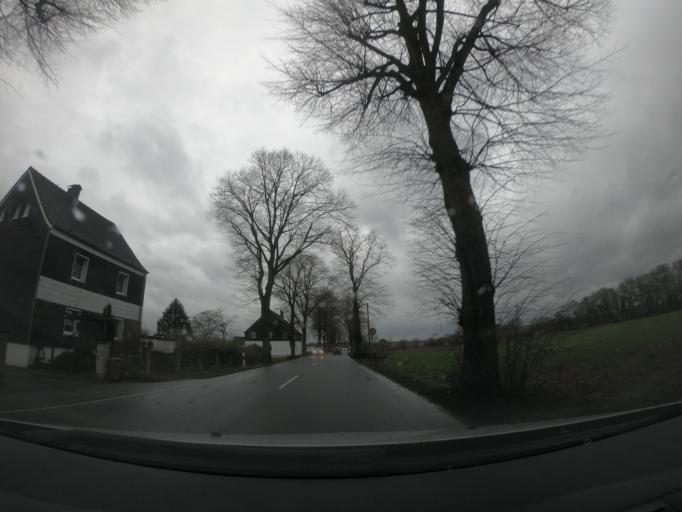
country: DE
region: North Rhine-Westphalia
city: Waltrop
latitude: 51.5945
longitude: 7.4228
